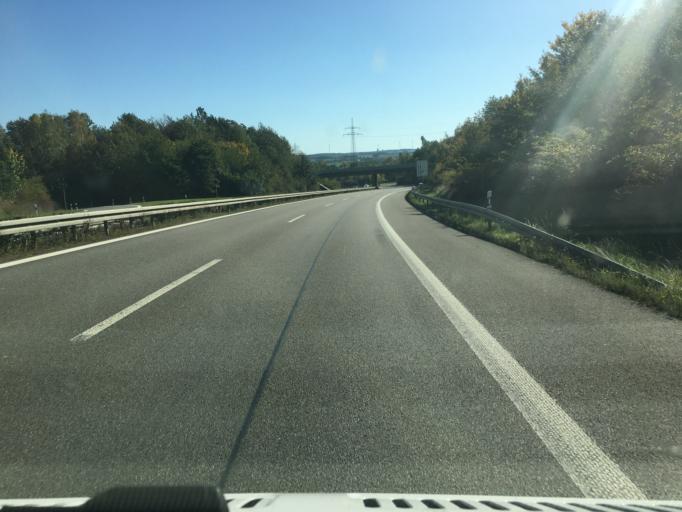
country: DE
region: Saxony
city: Dennheritz
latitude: 50.7899
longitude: 12.4746
